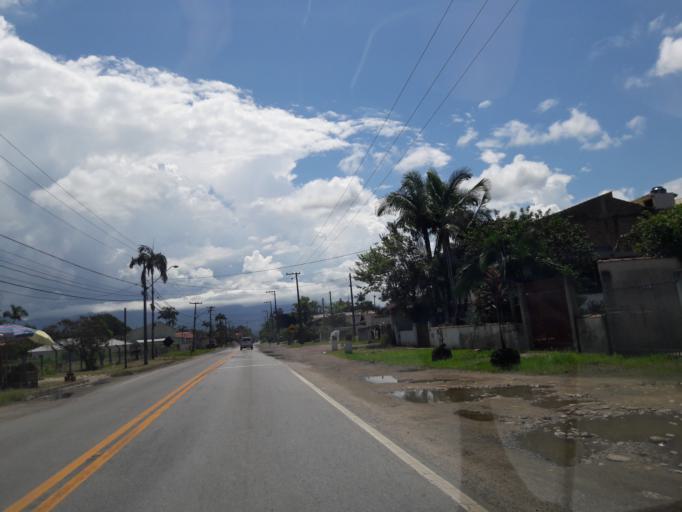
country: BR
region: Parana
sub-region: Antonina
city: Antonina
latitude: -25.4944
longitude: -48.8209
